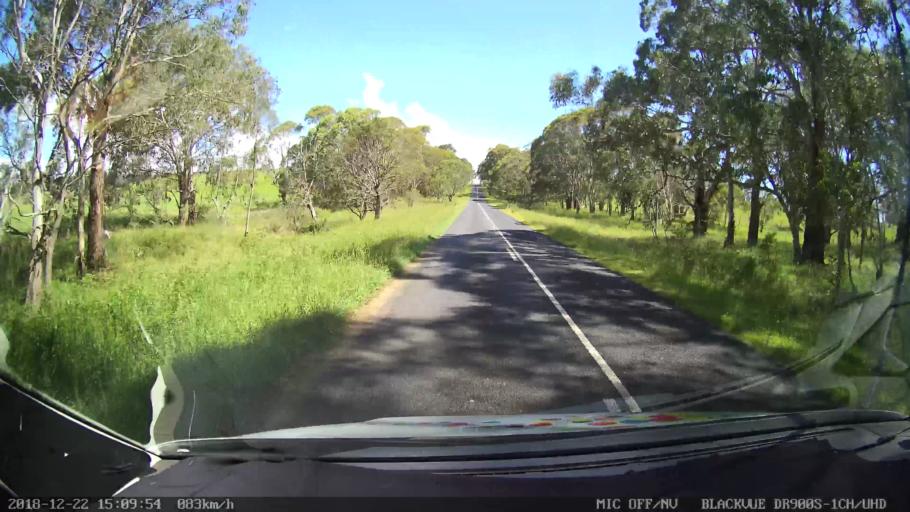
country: AU
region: New South Wales
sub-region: Bellingen
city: Dorrigo
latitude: -30.3288
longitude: 152.4060
